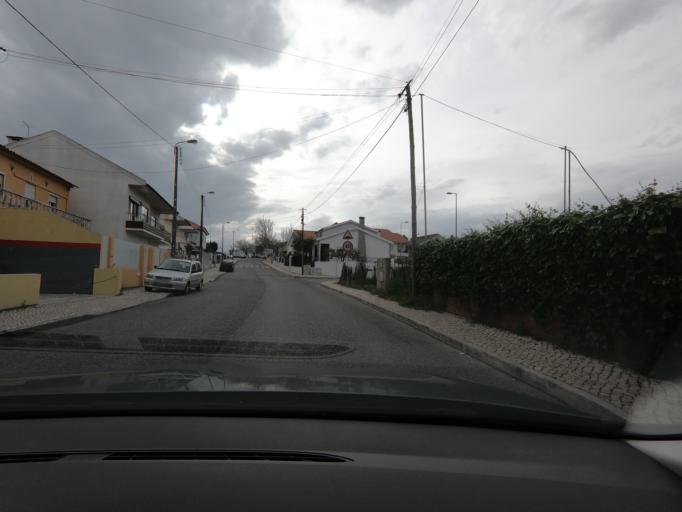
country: PT
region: Lisbon
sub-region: Cascais
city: Sao Domingos de Rana
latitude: 38.7126
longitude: -9.3372
